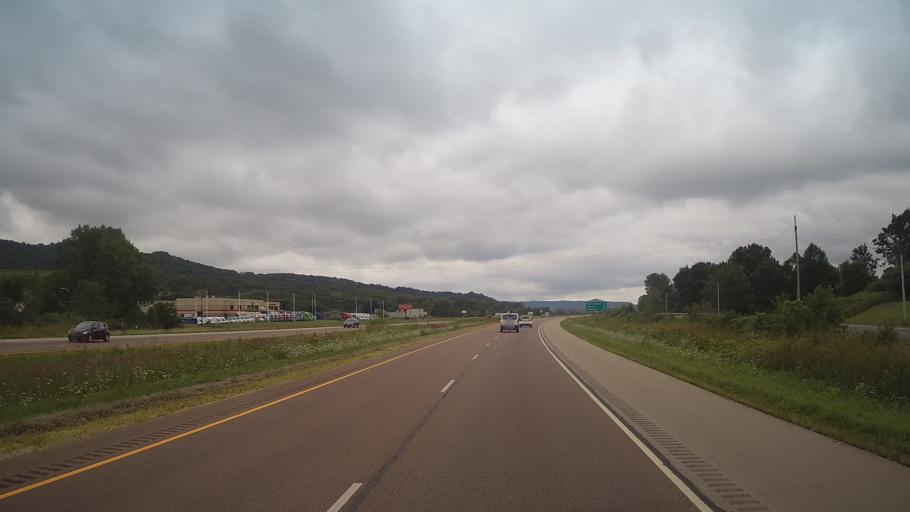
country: US
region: Wisconsin
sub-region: La Crosse County
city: Onalaska
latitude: 43.8754
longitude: -91.1684
